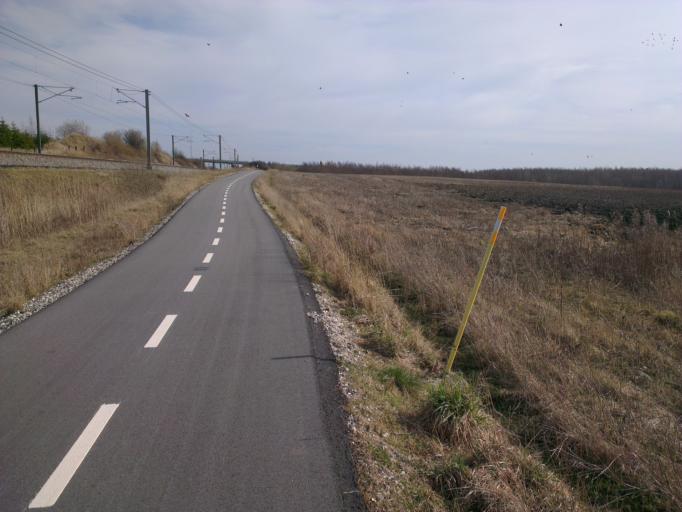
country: DK
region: Capital Region
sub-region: Frederikssund Kommune
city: Frederikssund
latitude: 55.8127
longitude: 12.0977
